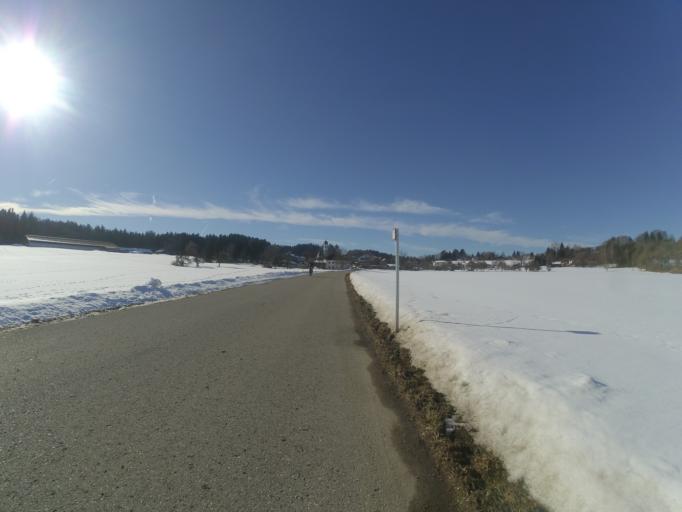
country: DE
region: Bavaria
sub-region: Upper Bavaria
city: Feldkirchen-Westerham
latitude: 47.9124
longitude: 11.8232
